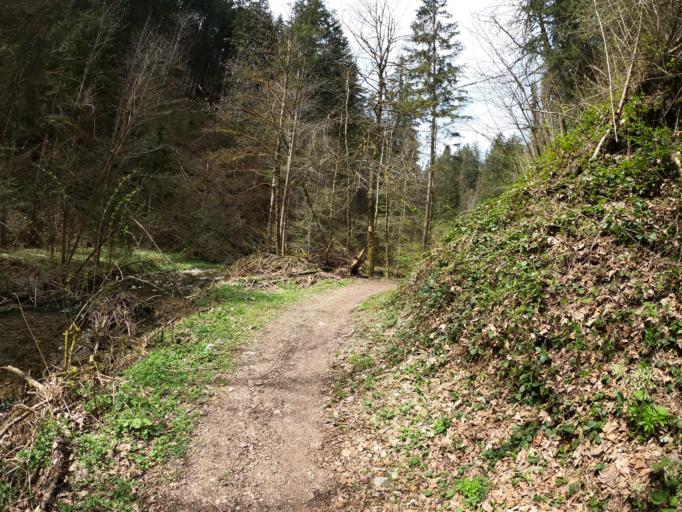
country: AT
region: Salzburg
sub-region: Politischer Bezirk Sankt Johann im Pongau
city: Pfarrwerfen
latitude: 47.4624
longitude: 13.2126
